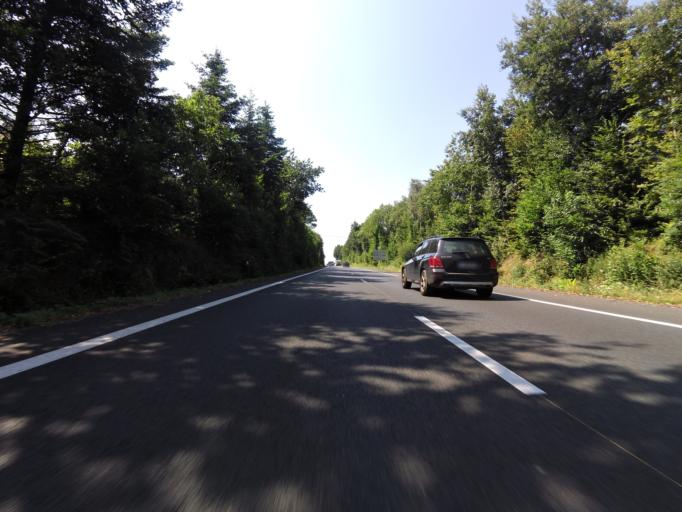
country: FR
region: Brittany
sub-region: Departement du Finistere
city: Plomelin
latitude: 47.9656
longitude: -4.1487
